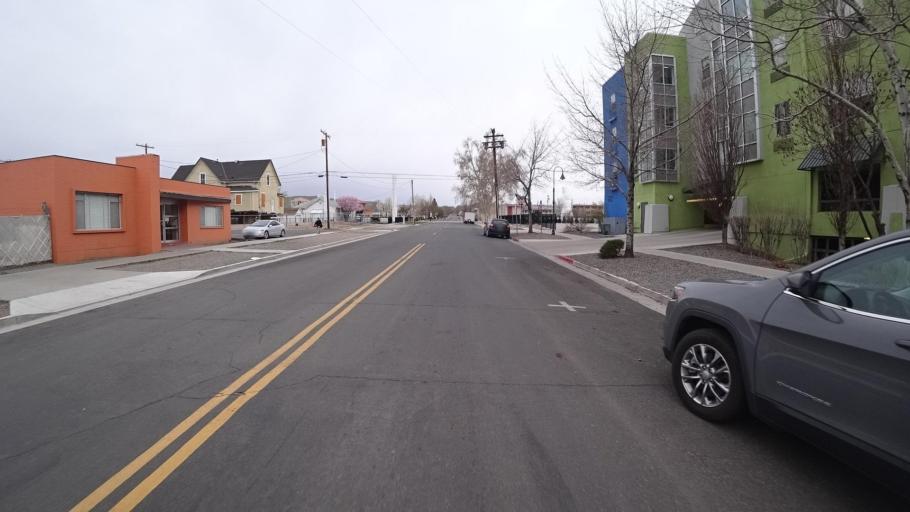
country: US
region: Nevada
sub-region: Washoe County
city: Reno
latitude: 39.5271
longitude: -119.8231
